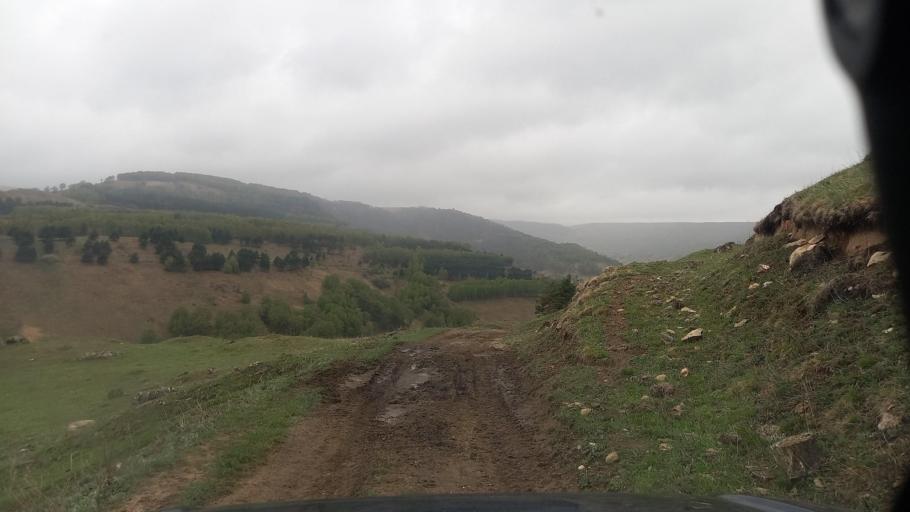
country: RU
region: Stavropol'skiy
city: Nezhinskiy
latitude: 43.8477
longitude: 42.6330
